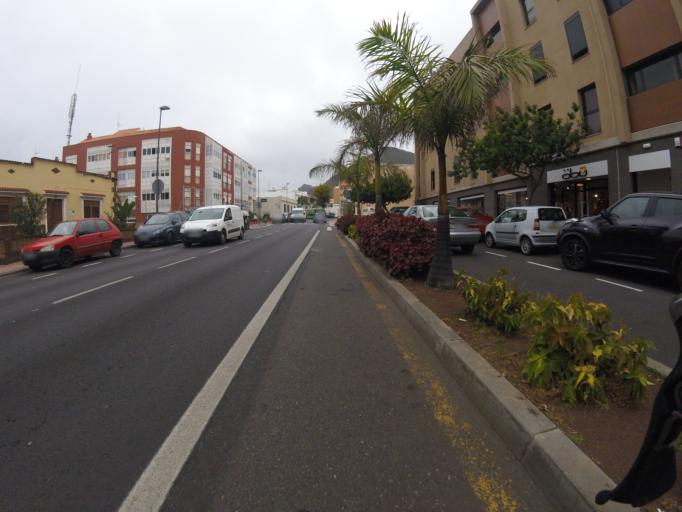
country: ES
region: Canary Islands
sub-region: Provincia de Santa Cruz de Tenerife
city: Tegueste
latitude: 28.5336
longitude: -16.3644
